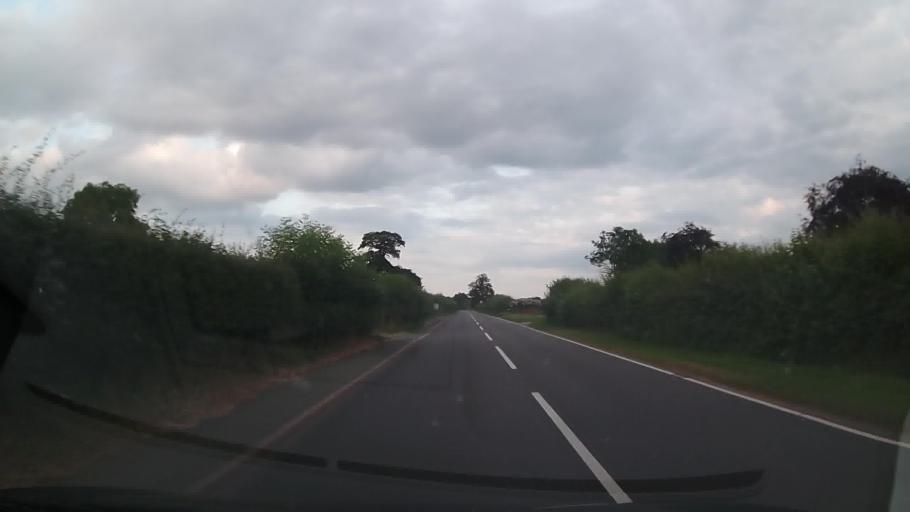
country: GB
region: England
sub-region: Shropshire
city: Great Ness
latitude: 52.7942
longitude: -2.8646
